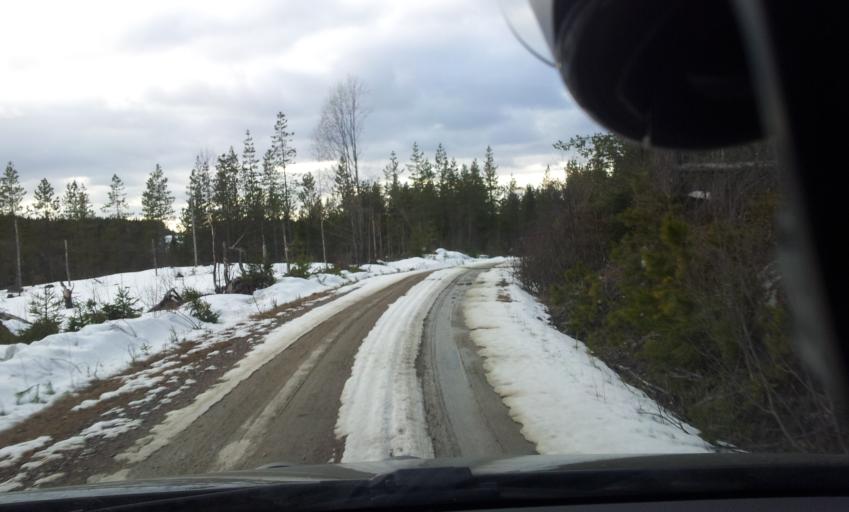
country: SE
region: Vaesternorrland
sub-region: Ange Kommun
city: Ange
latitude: 62.1930
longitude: 15.7583
